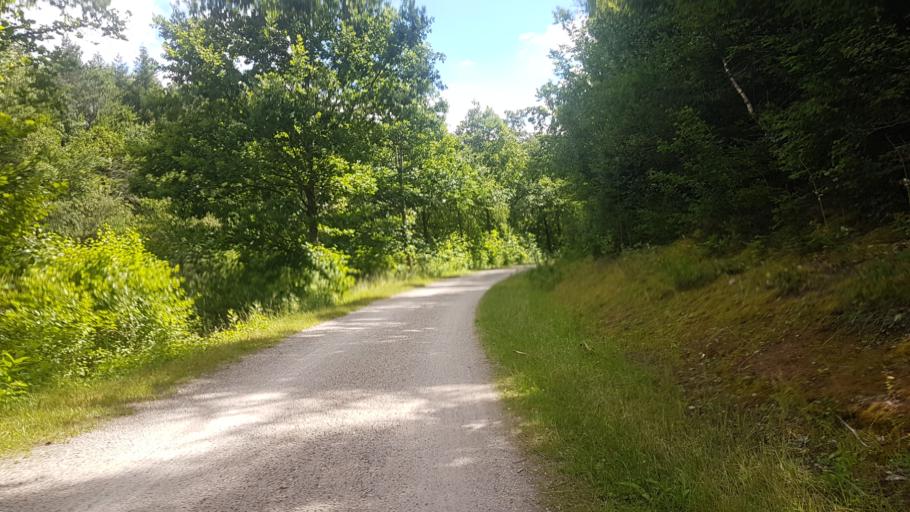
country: DE
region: Bavaria
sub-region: Regierungsbezirk Mittelfranken
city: Gunzenhausen
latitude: 49.1279
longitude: 10.7838
